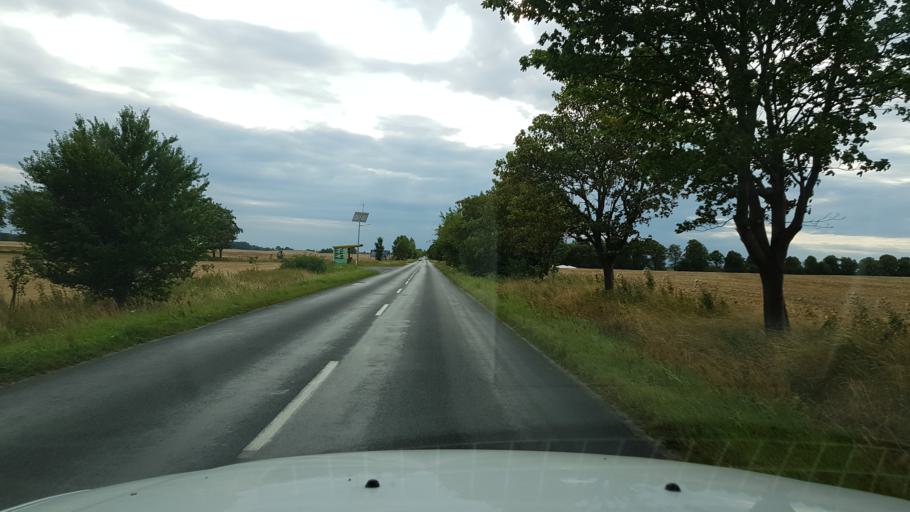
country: PL
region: West Pomeranian Voivodeship
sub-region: Powiat kolobrzeski
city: Dygowo
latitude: 54.1472
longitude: 15.6682
